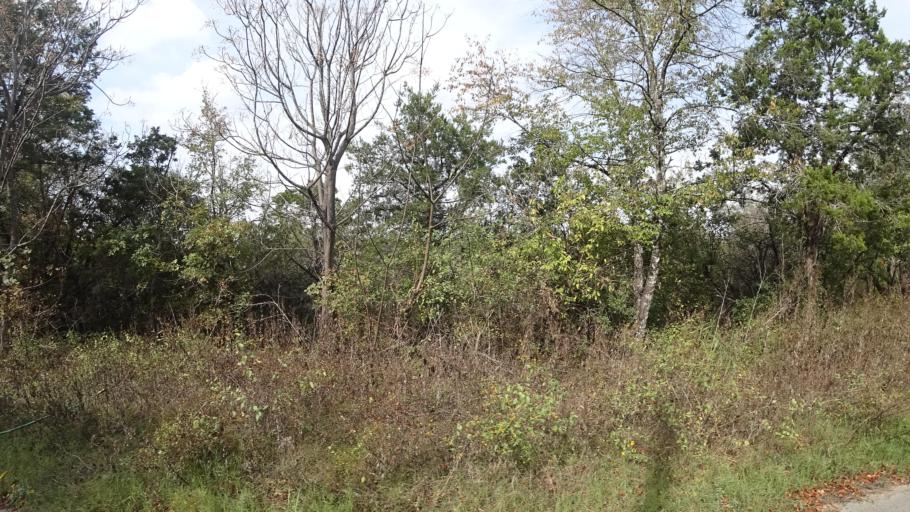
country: US
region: Texas
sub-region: Travis County
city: Hudson Bend
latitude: 30.3805
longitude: -97.9272
